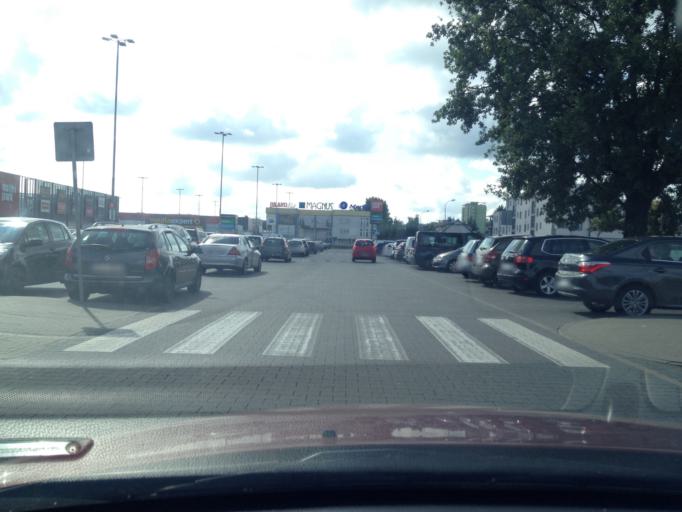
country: PL
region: West Pomeranian Voivodeship
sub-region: Szczecin
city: Szczecin
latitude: 53.3813
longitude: 14.6692
